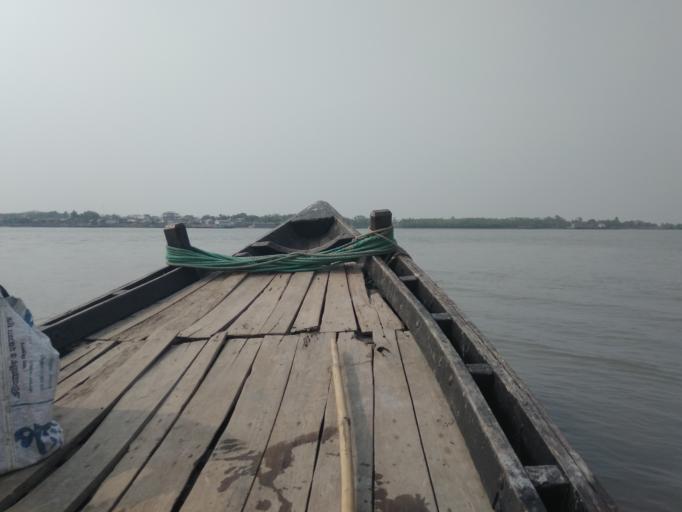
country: IN
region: West Bengal
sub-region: North 24 Parganas
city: Taki
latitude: 22.3471
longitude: 89.2078
